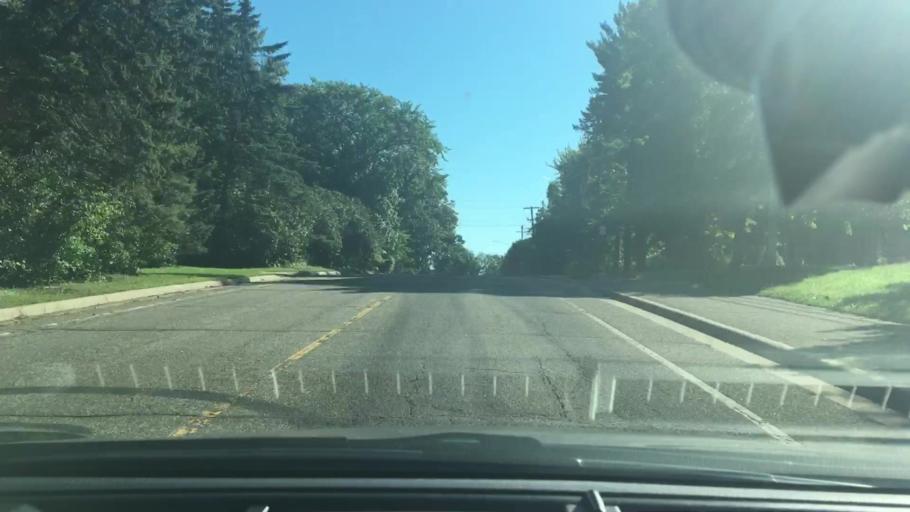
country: US
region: Minnesota
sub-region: Hennepin County
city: Minnetonka Mills
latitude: 44.9787
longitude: -93.4229
